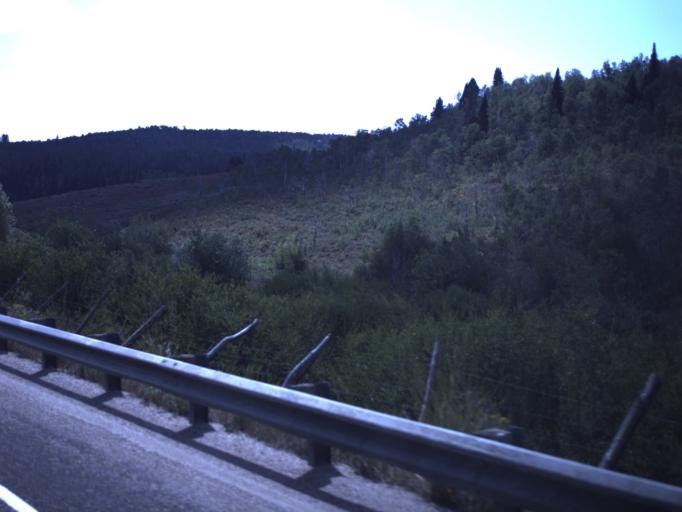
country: US
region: Utah
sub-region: Cache County
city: Richmond
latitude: 41.9153
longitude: -111.5624
